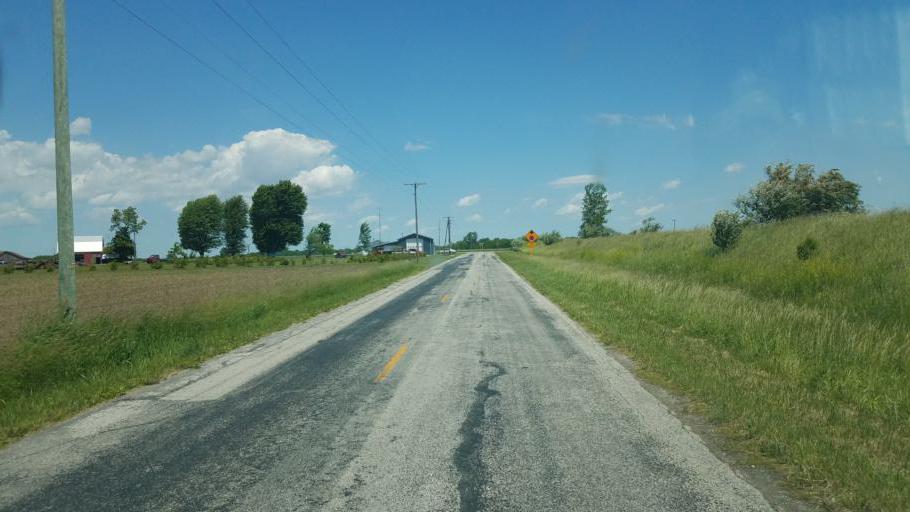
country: US
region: Ohio
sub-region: Hardin County
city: Forest
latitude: 40.6806
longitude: -83.4198
